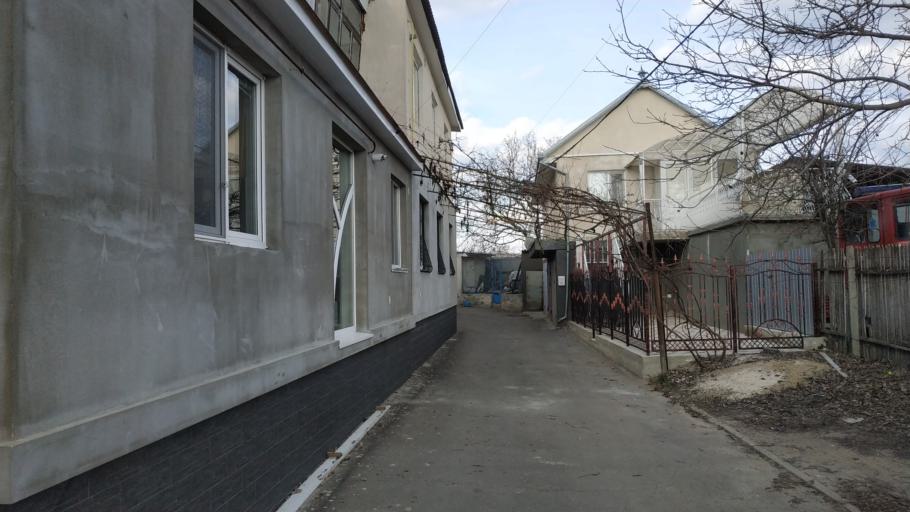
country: MD
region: Hincesti
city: Hincesti
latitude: 46.8328
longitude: 28.5837
